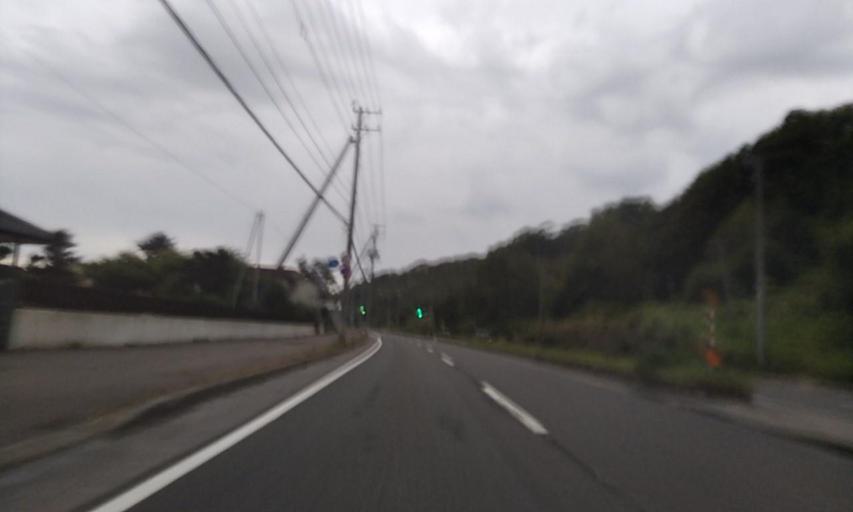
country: JP
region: Hokkaido
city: Abashiri
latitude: 43.9845
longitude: 144.2959
